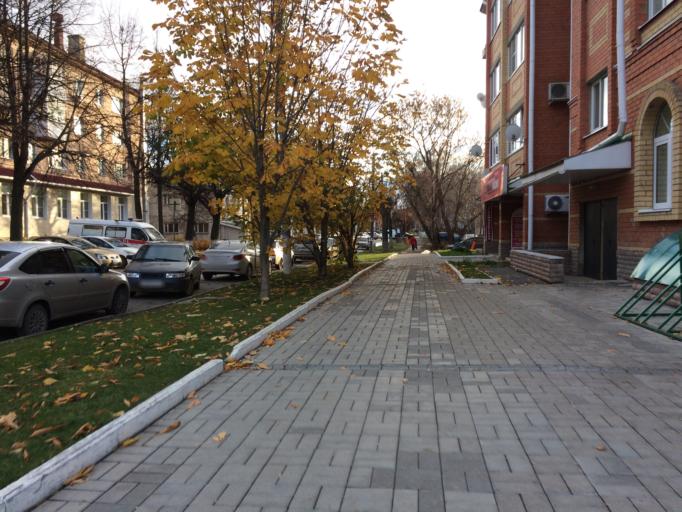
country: RU
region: Mariy-El
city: Yoshkar-Ola
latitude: 56.6396
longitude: 47.8980
